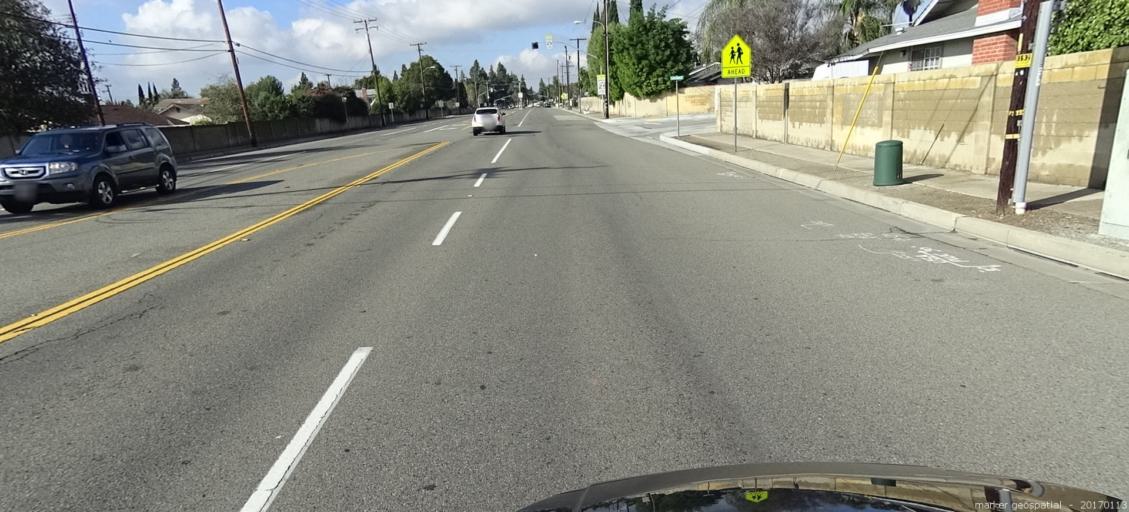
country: US
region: California
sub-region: Orange County
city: Placentia
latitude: 33.8894
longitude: -117.8503
